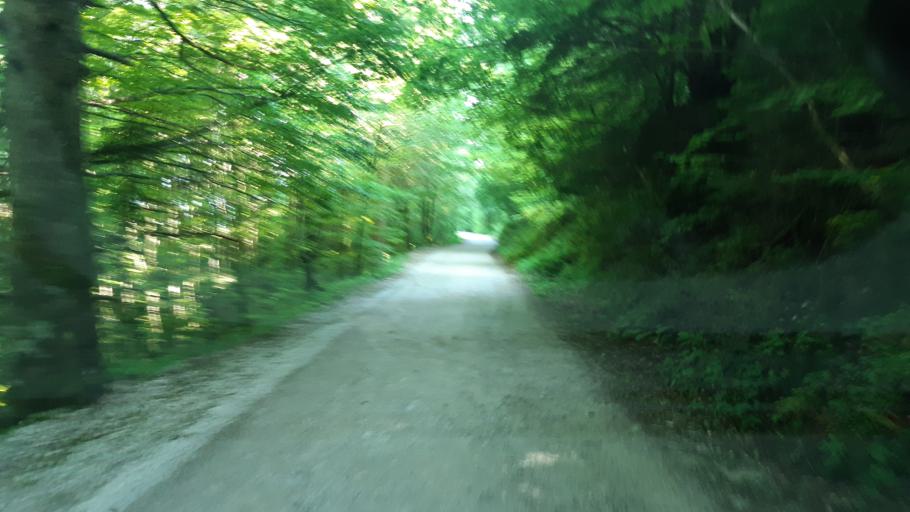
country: SI
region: Trzic
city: Bistrica pri Trzicu
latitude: 46.3685
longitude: 14.2779
